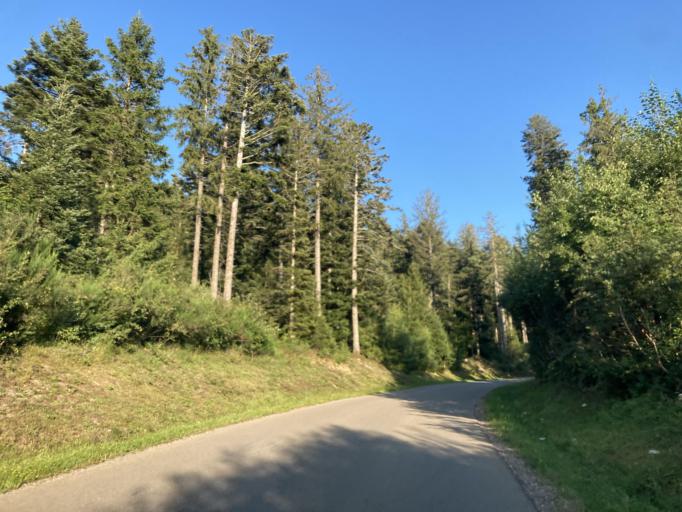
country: DE
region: Baden-Wuerttemberg
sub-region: Freiburg Region
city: Schonach im Schwarzwald
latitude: 48.1702
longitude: 8.1828
